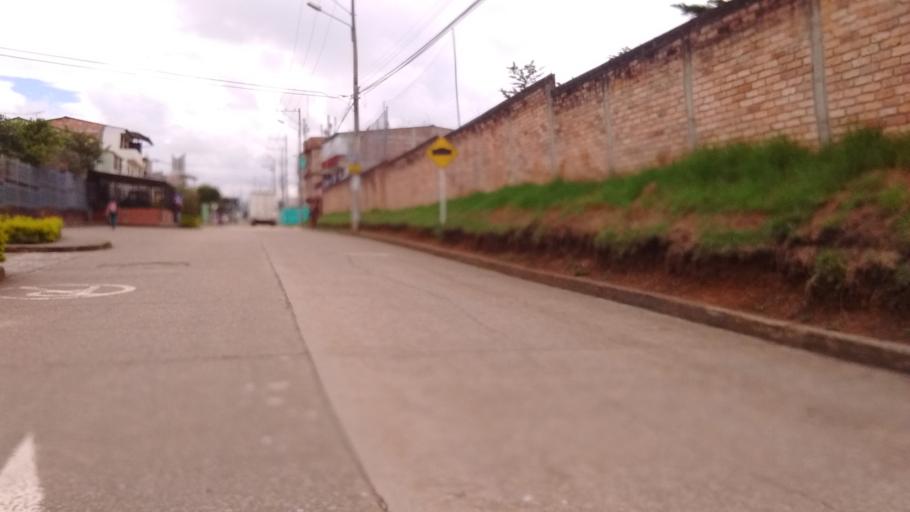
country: CO
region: Cauca
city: Popayan
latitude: 2.4800
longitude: -76.5779
